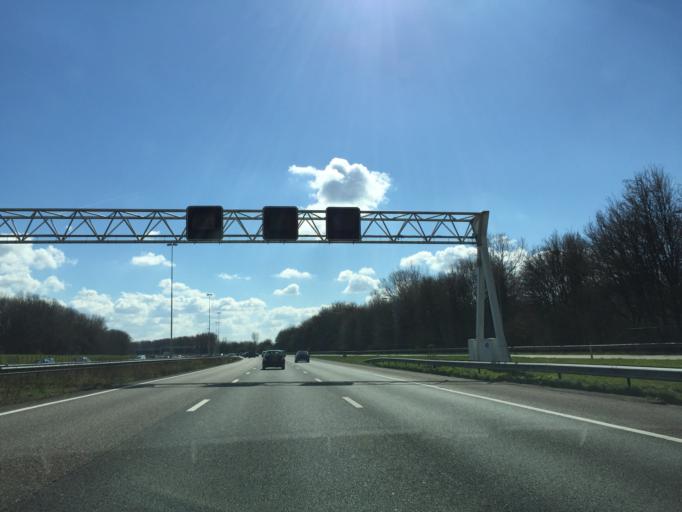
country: NL
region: South Holland
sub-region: Gemeente Strijen
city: Strijen
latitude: 51.7323
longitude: 4.6324
